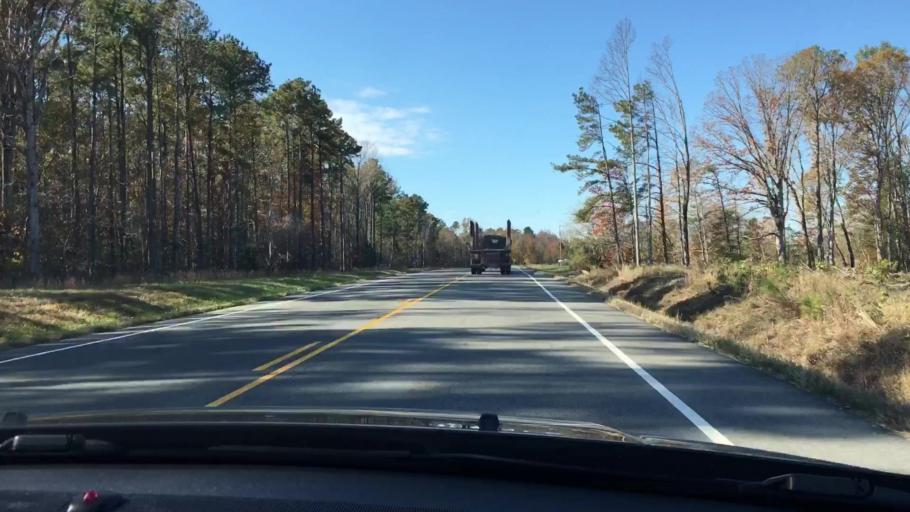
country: US
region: Virginia
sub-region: King William County
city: Central Garage
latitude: 37.7883
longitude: -77.1792
